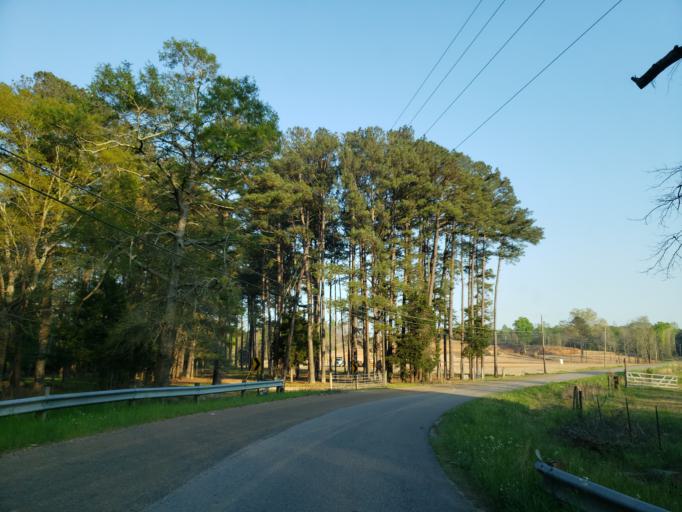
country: US
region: Mississippi
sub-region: Lauderdale County
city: Marion
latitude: 32.4032
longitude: -88.5916
